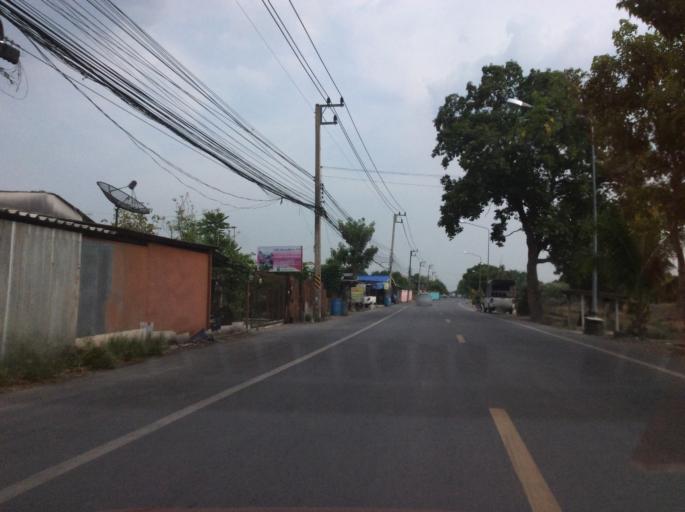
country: TH
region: Pathum Thani
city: Lam Luk Ka
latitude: 13.9600
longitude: 100.7275
